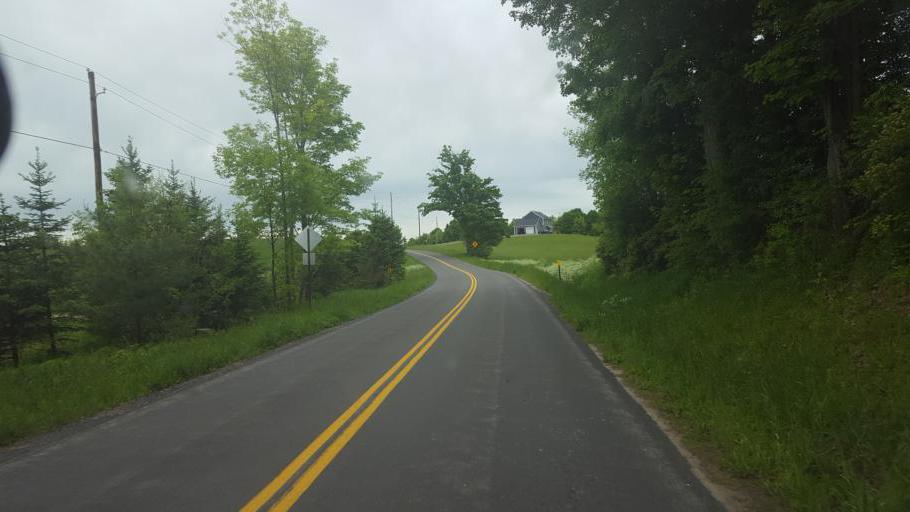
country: US
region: New York
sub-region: Herkimer County
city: Frankfort
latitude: 42.9215
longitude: -75.1370
